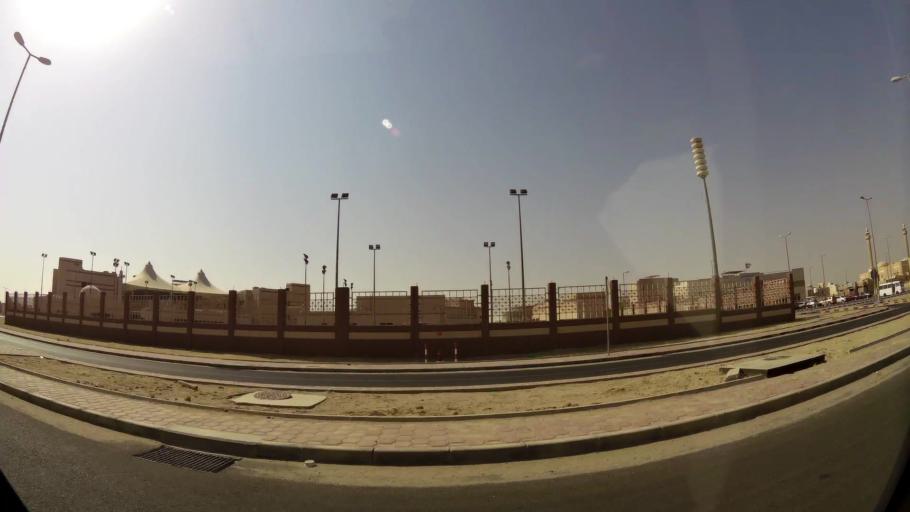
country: KW
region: Al Ahmadi
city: Al Wafrah
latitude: 28.8001
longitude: 48.0703
